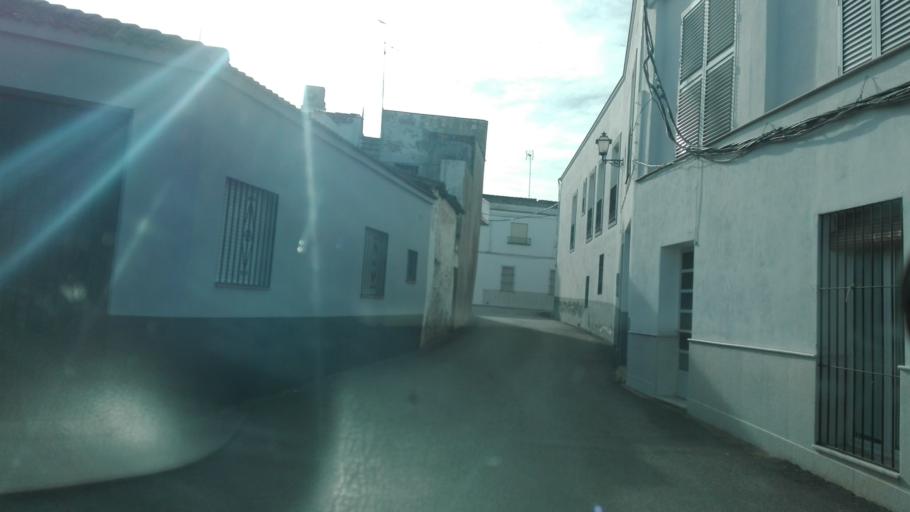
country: ES
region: Extremadura
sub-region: Provincia de Badajoz
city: Usagre
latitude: 38.3564
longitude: -6.1683
